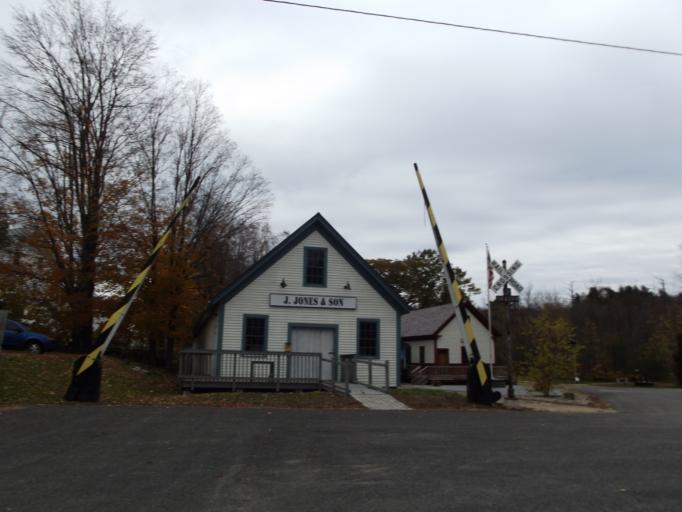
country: US
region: New Hampshire
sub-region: Strafford County
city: New Durham
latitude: 43.4562
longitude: -71.2195
